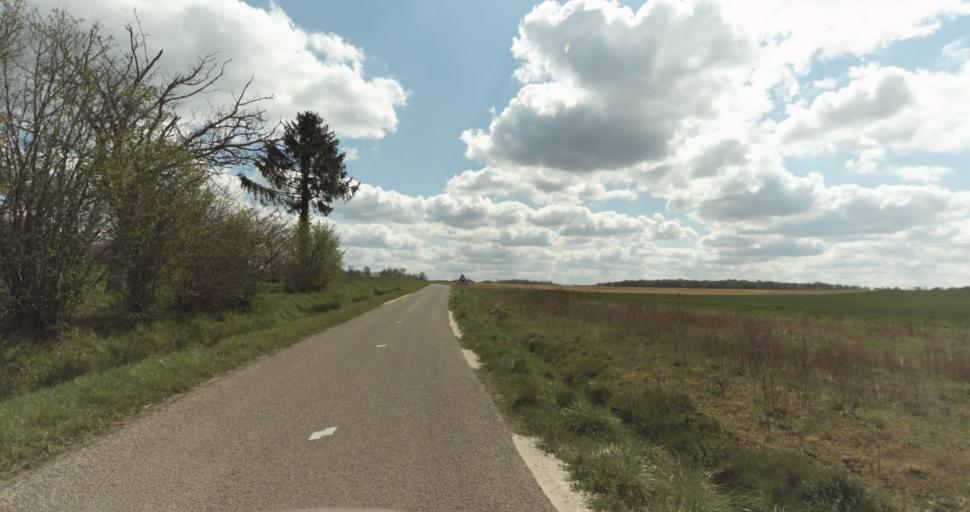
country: FR
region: Bourgogne
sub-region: Departement de la Cote-d'Or
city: Auxonne
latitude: 47.1843
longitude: 5.4099
